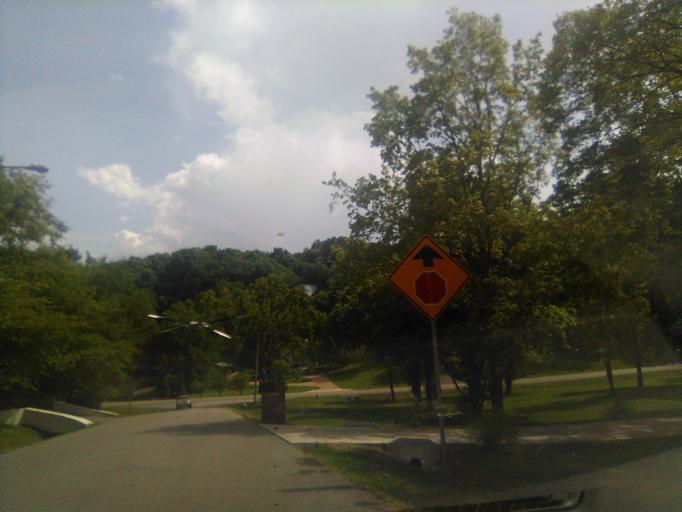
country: US
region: Tennessee
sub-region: Davidson County
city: Belle Meade
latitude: 36.0969
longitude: -86.8914
